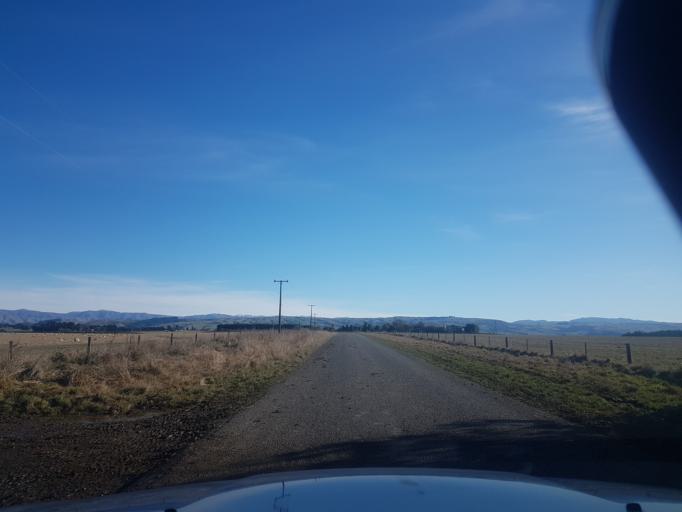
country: NZ
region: Canterbury
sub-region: Timaru District
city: Pleasant Point
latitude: -44.2545
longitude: 171.0311
